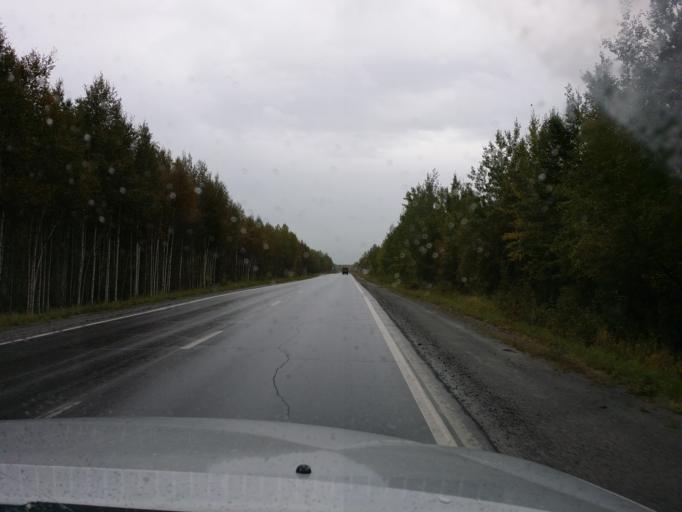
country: RU
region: Khanty-Mansiyskiy Avtonomnyy Okrug
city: Langepas
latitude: 61.1659
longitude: 75.5824
